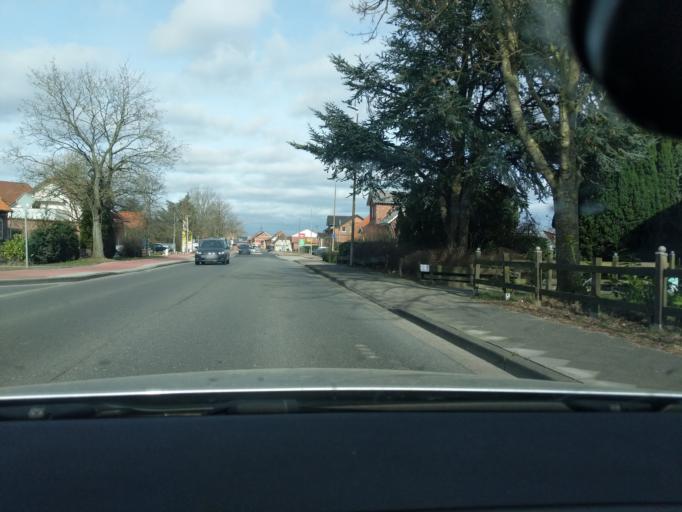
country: DE
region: Lower Saxony
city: Stade
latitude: 53.6493
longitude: 9.4816
